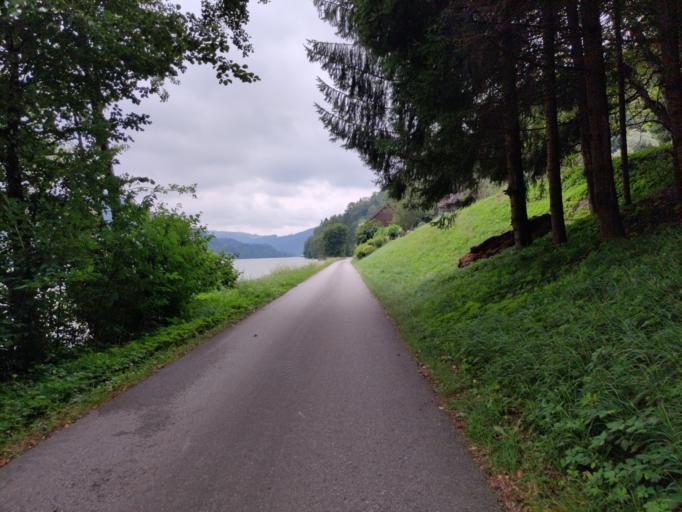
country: AT
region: Lower Austria
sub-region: Politischer Bezirk Melk
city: Nochling
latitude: 48.2218
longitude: 14.9460
